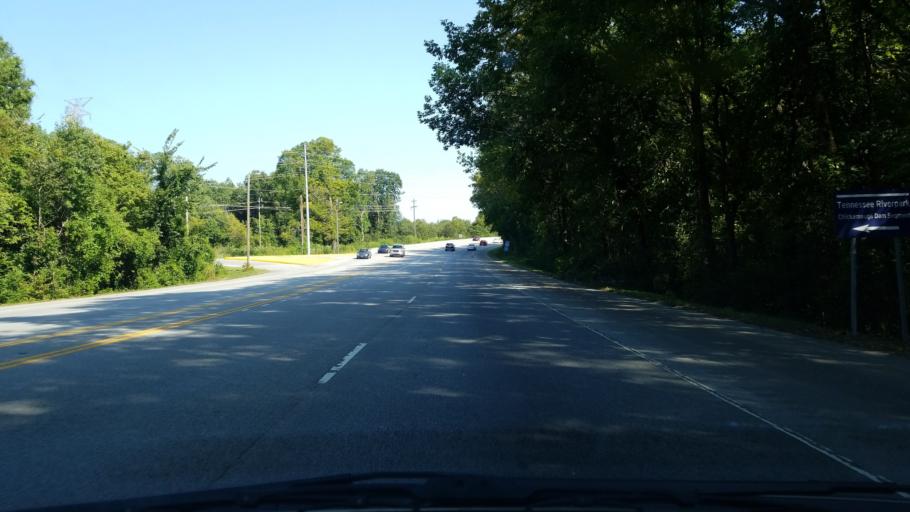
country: US
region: Tennessee
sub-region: Hamilton County
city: East Chattanooga
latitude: 35.0931
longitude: -85.2283
